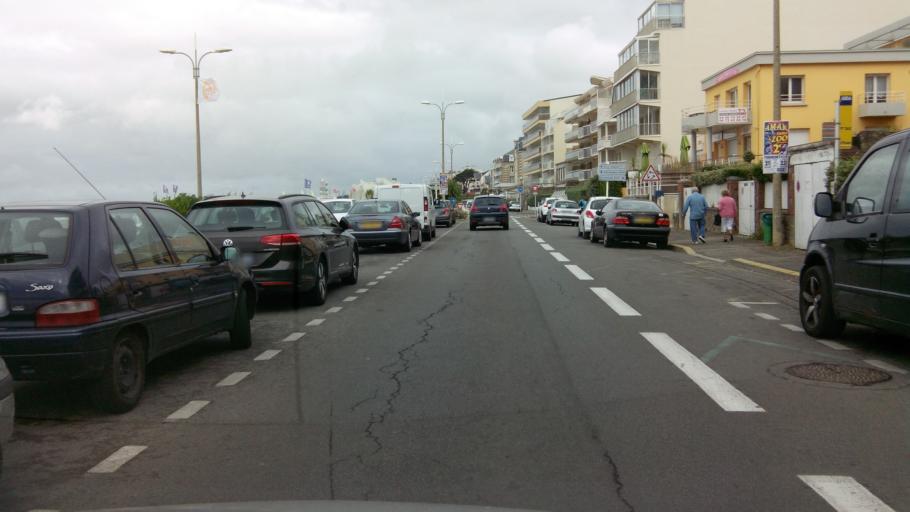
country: FR
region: Pays de la Loire
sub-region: Departement de la Loire-Atlantique
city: Pornichet
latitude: 47.2671
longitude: -2.3472
